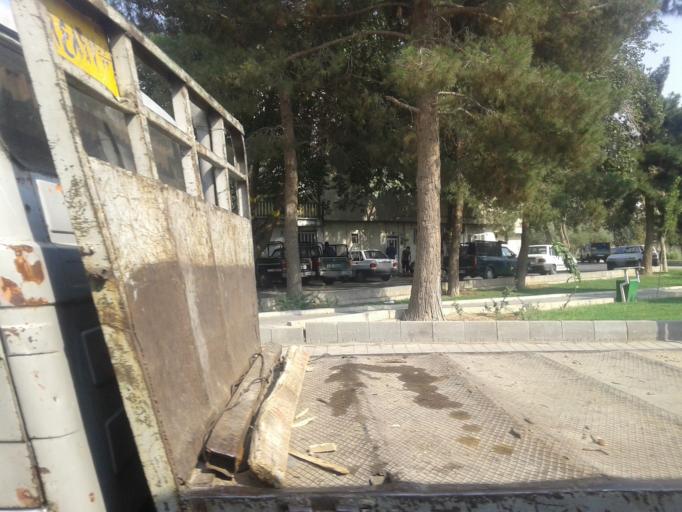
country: IR
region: Tehran
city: Eslamshahr
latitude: 35.6418
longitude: 51.3010
